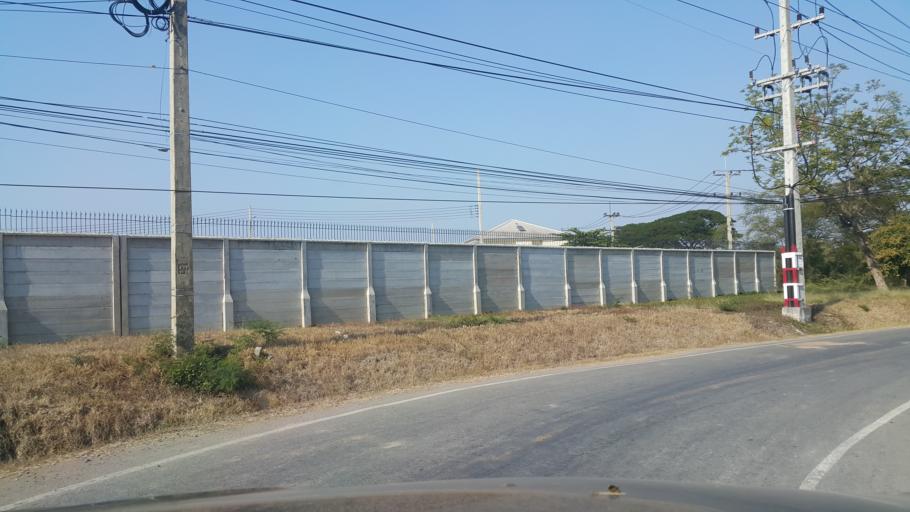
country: TH
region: Khon Kaen
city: Khon Kaen
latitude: 16.4041
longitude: 102.8802
